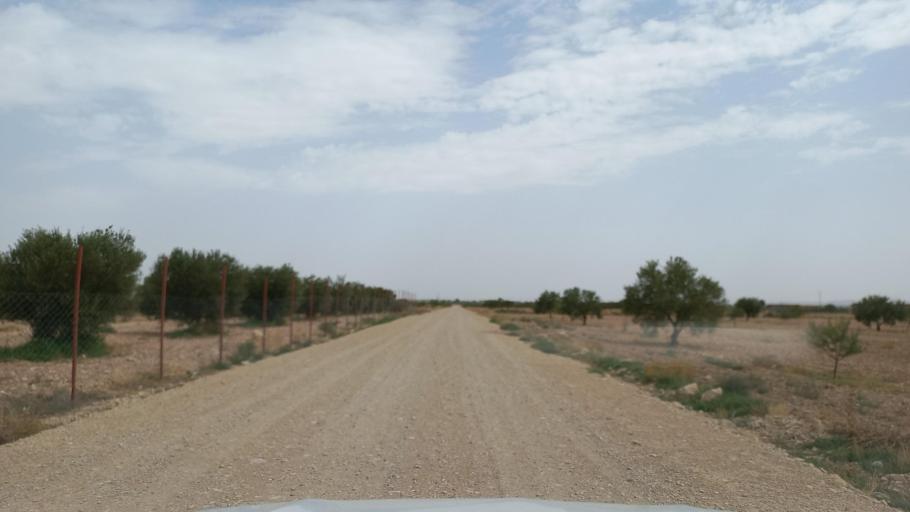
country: TN
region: Al Qasrayn
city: Kasserine
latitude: 35.2797
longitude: 9.0136
